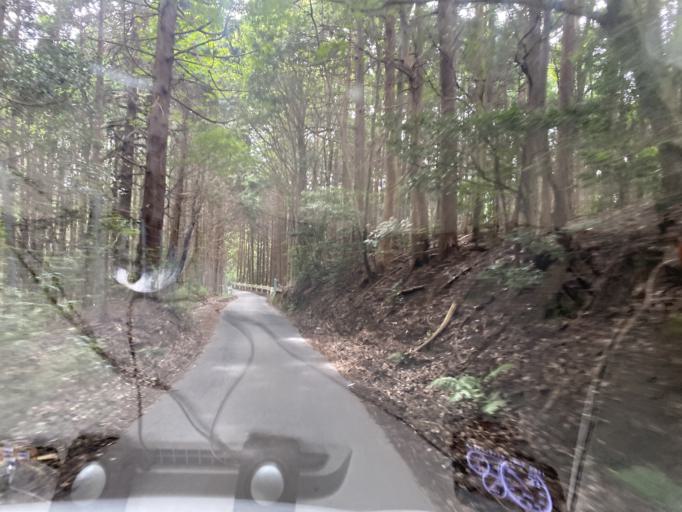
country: JP
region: Nara
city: Nara-shi
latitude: 34.6797
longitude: 135.8925
